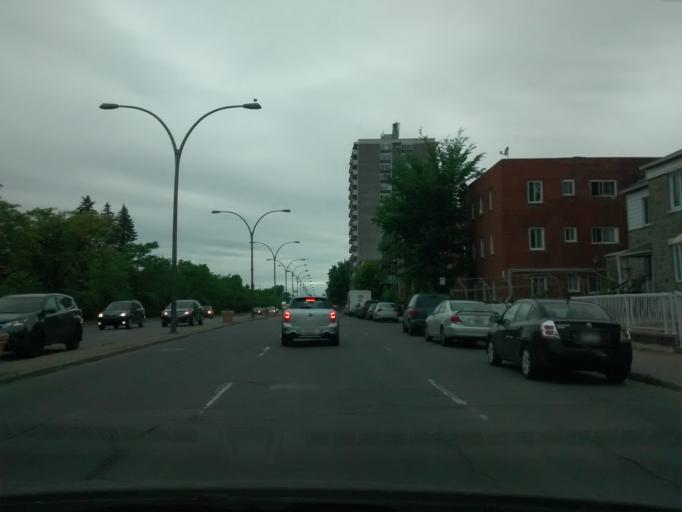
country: CA
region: Quebec
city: Mont-Royal
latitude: 45.5253
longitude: -73.6298
